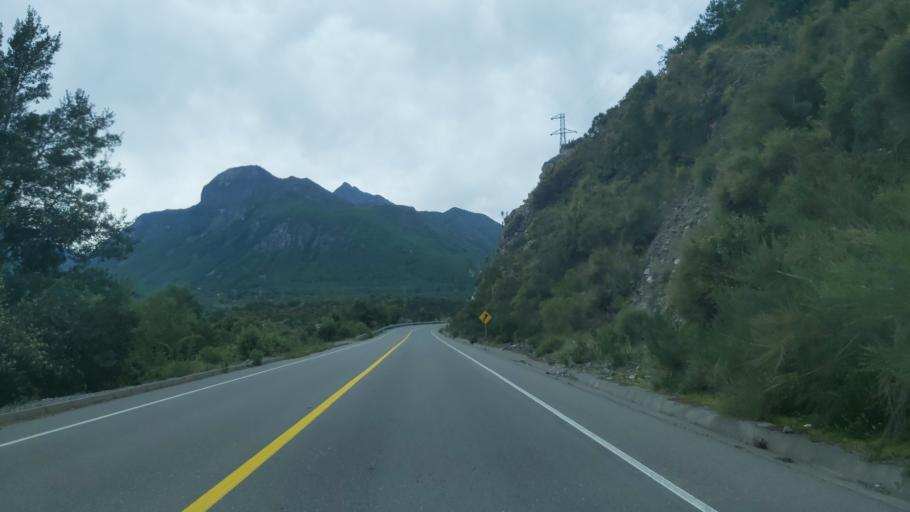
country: CL
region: Maule
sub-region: Provincia de Linares
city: Colbun
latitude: -35.7087
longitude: -71.0834
